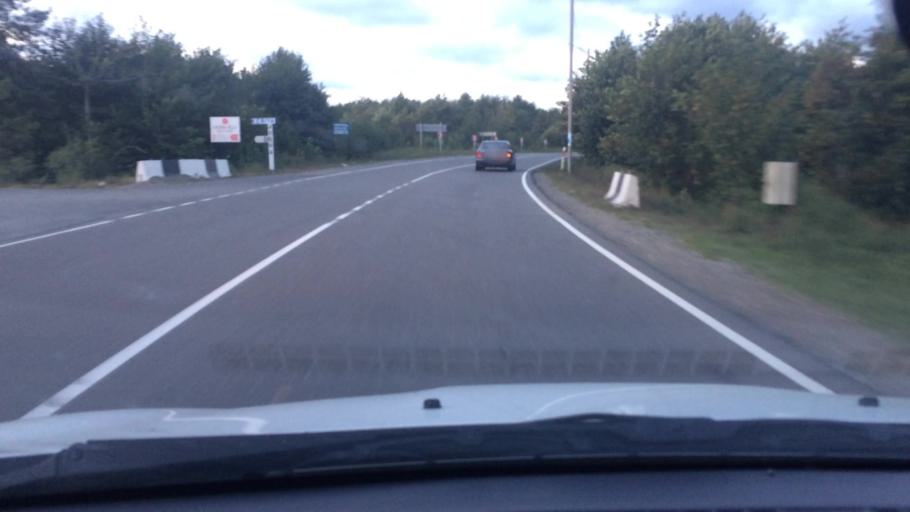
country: GE
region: Guria
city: Urek'i
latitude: 41.9663
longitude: 41.7734
